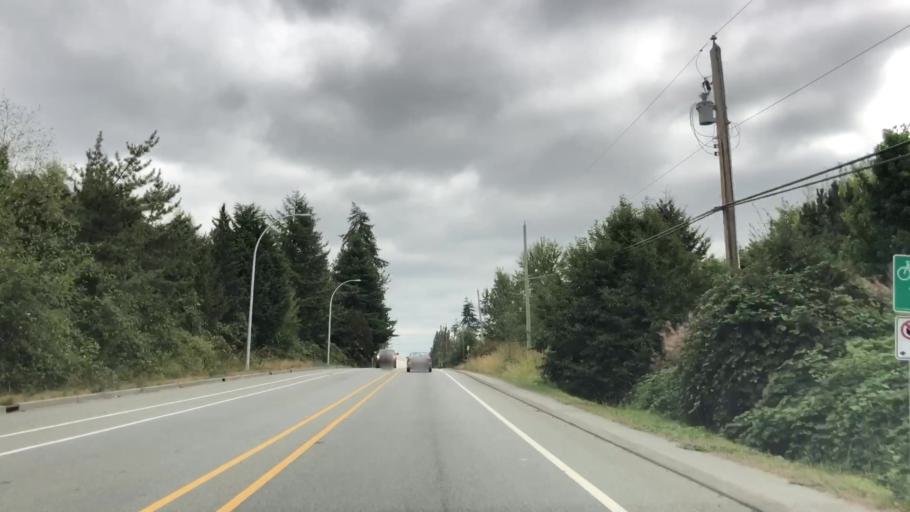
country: CA
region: British Columbia
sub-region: Greater Vancouver Regional District
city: White Rock
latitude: 49.0601
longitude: -122.7735
